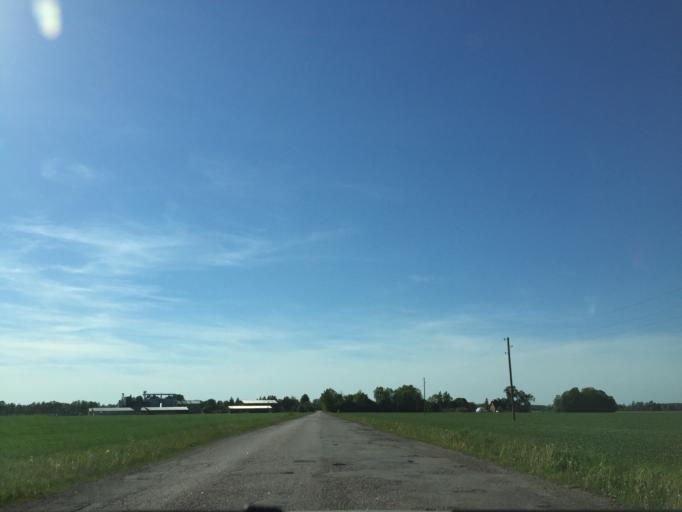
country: LV
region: Jelgava
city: Jelgava
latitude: 56.5229
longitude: 23.7258
